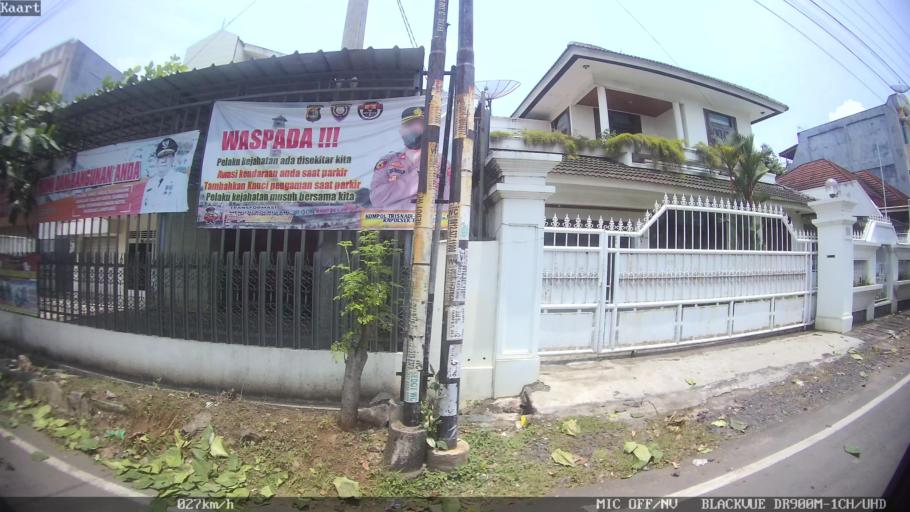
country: ID
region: Lampung
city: Bandarlampung
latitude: -5.4403
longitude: 105.2698
